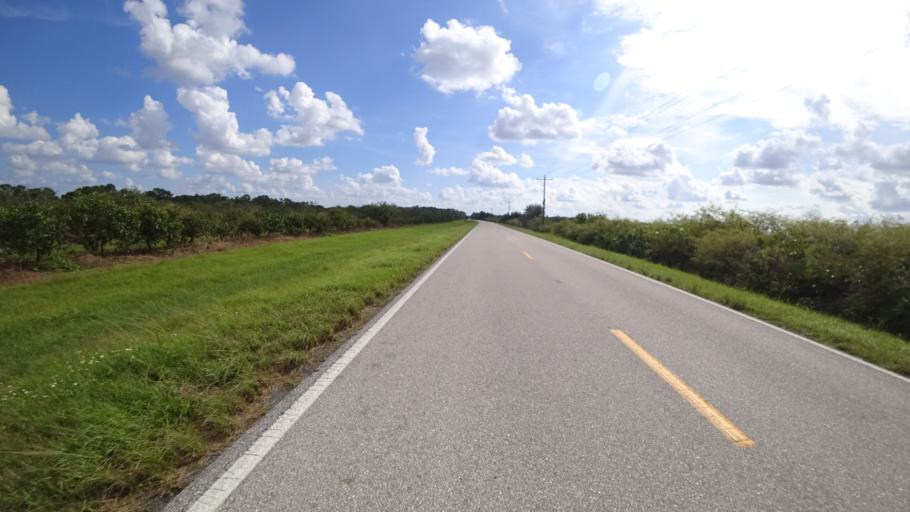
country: US
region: Florida
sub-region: Hillsborough County
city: Wimauma
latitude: 27.5756
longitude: -82.1045
